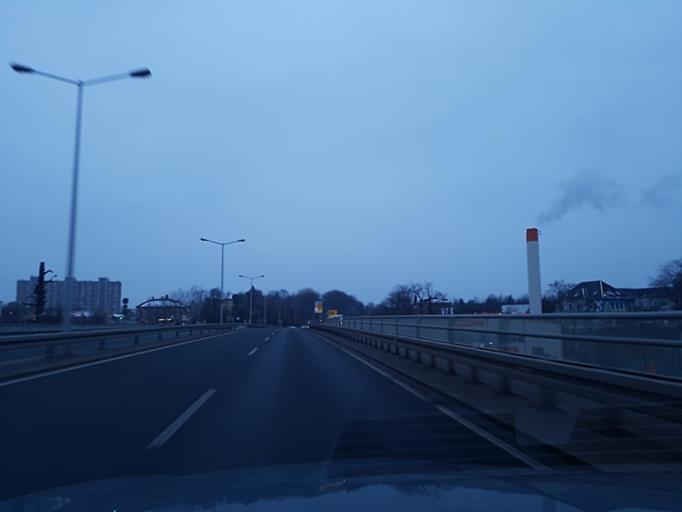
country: DE
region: Saxony
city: Riesa
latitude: 51.3105
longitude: 13.2950
